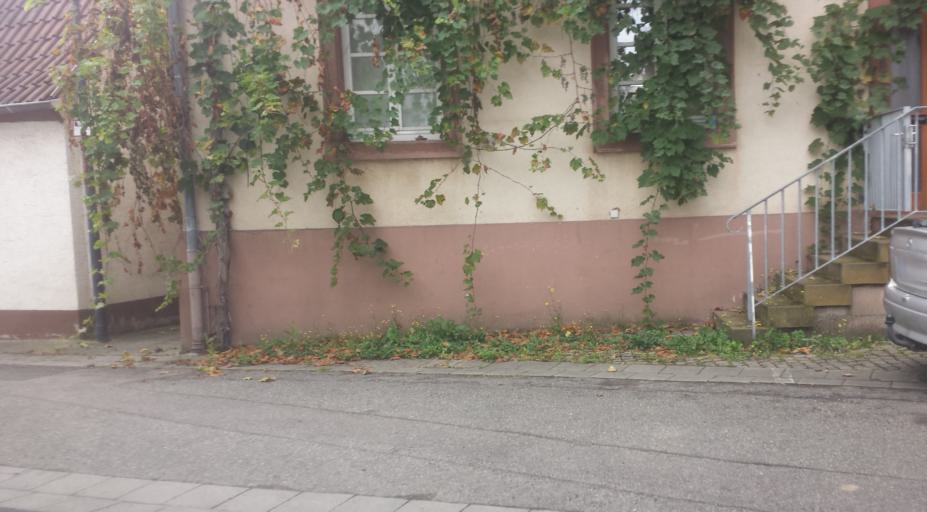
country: DE
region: Rheinland-Pfalz
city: Bornheim
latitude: 49.2202
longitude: 8.1500
